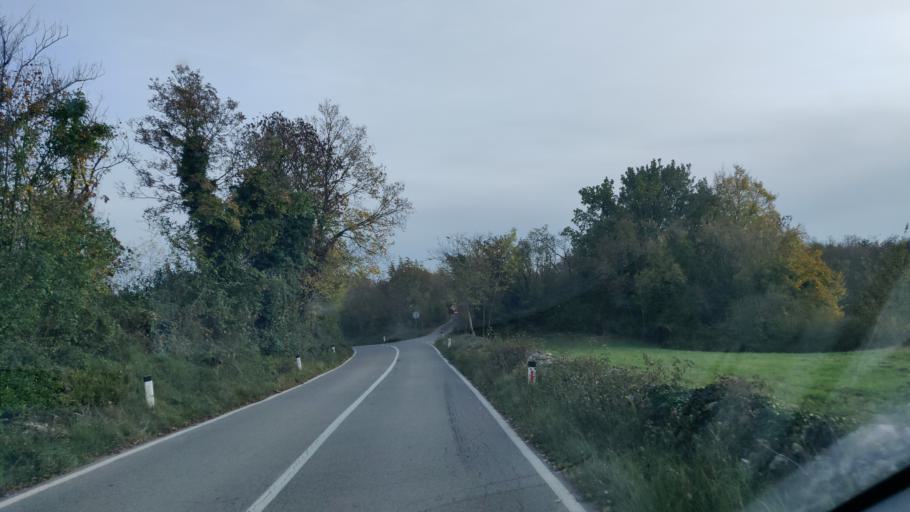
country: SI
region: Rence-Vogrsko
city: Rence
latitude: 45.8296
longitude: 13.6661
